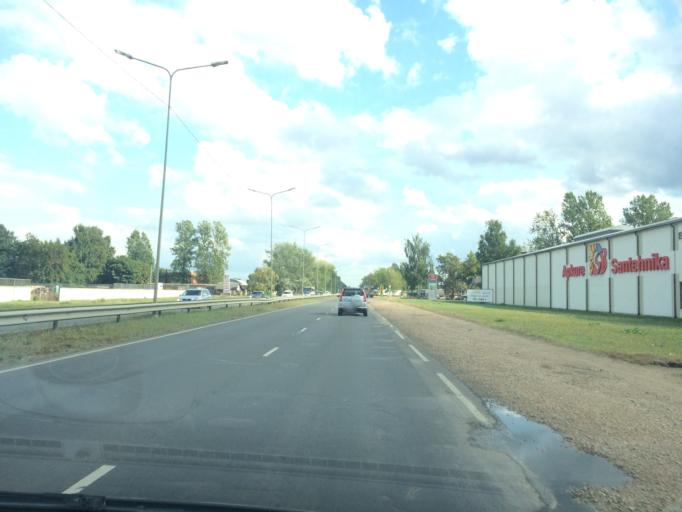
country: LV
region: Kekava
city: Kekava
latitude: 56.8907
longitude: 24.2252
